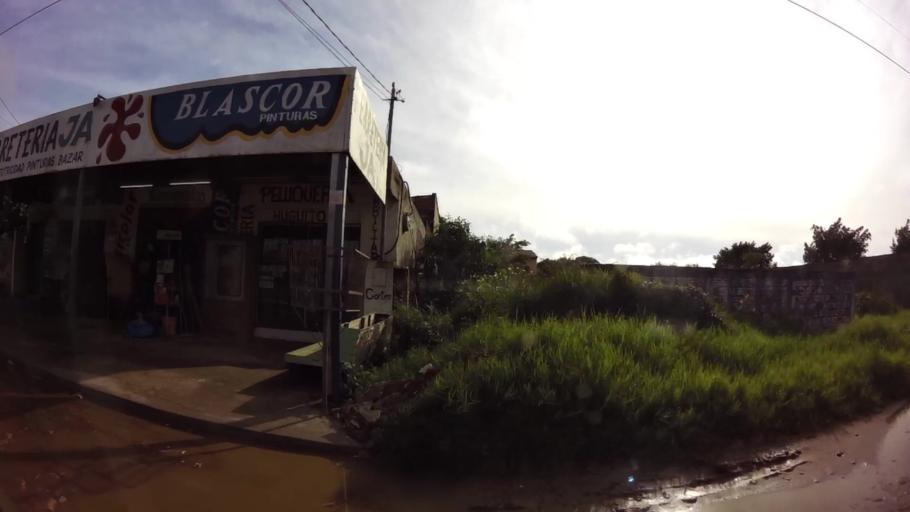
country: PY
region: Central
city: Limpio
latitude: -25.1822
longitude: -57.4901
